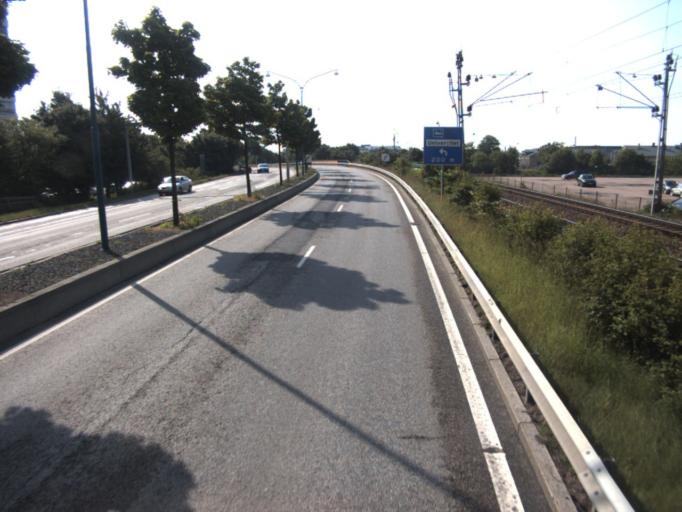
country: SE
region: Skane
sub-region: Helsingborg
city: Helsingborg
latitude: 56.0363
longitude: 12.7024
